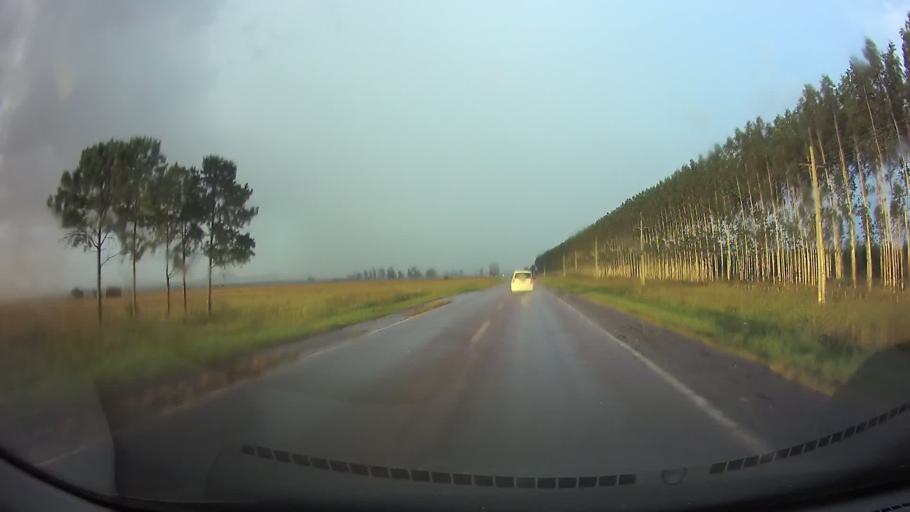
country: PY
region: Paraguari
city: Paraguari
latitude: -25.6678
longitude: -57.1644
